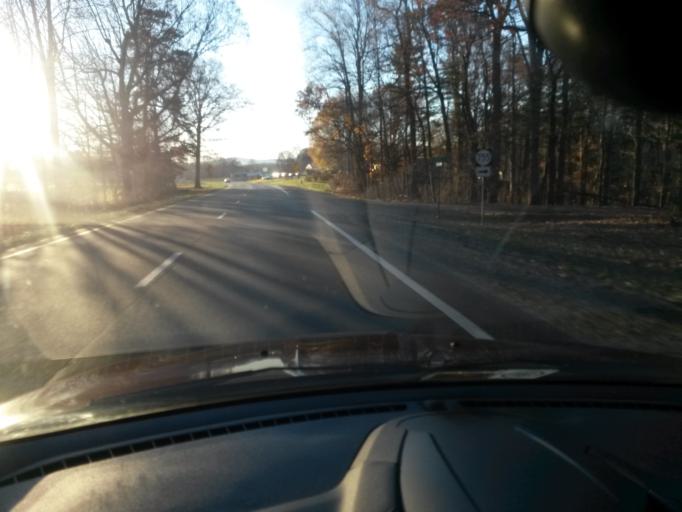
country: US
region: Virginia
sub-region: Franklin County
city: Henry Fork
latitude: 36.9422
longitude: -79.8765
